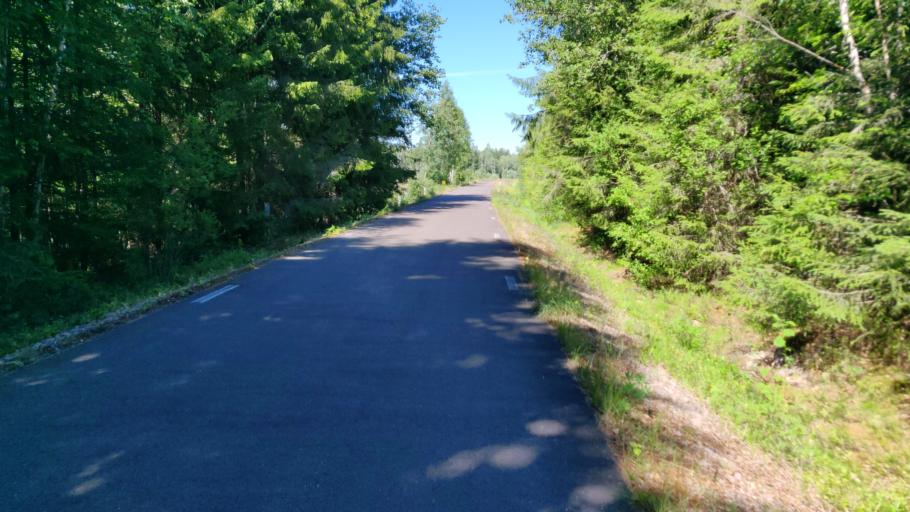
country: SE
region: Vaermland
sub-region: Hagfors Kommun
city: Hagfors
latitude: 59.9733
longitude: 13.5724
